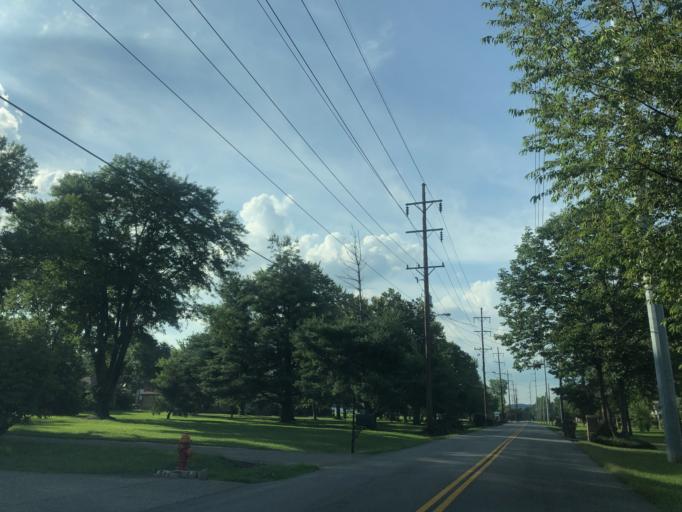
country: US
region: Tennessee
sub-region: Davidson County
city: Nashville
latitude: 36.2404
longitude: -86.8280
